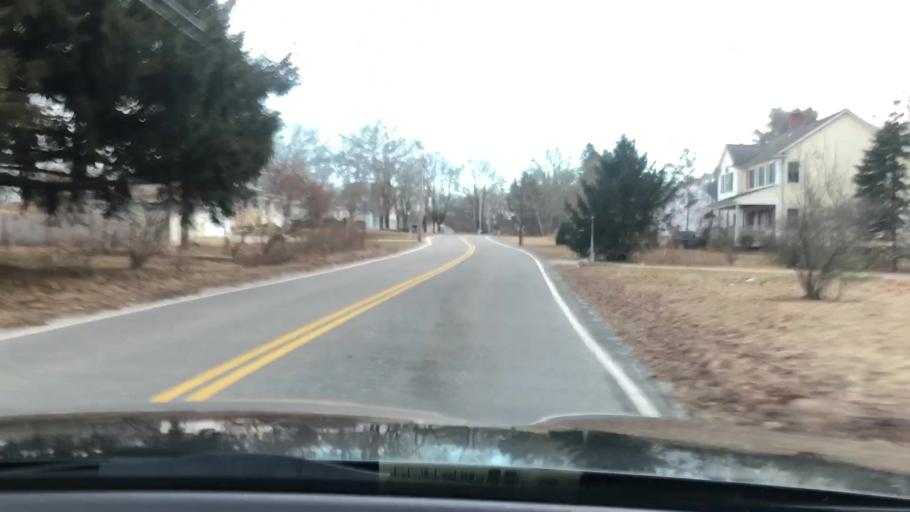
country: US
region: Massachusetts
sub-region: Worcester County
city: Blackstone
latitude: 42.0428
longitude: -71.5241
